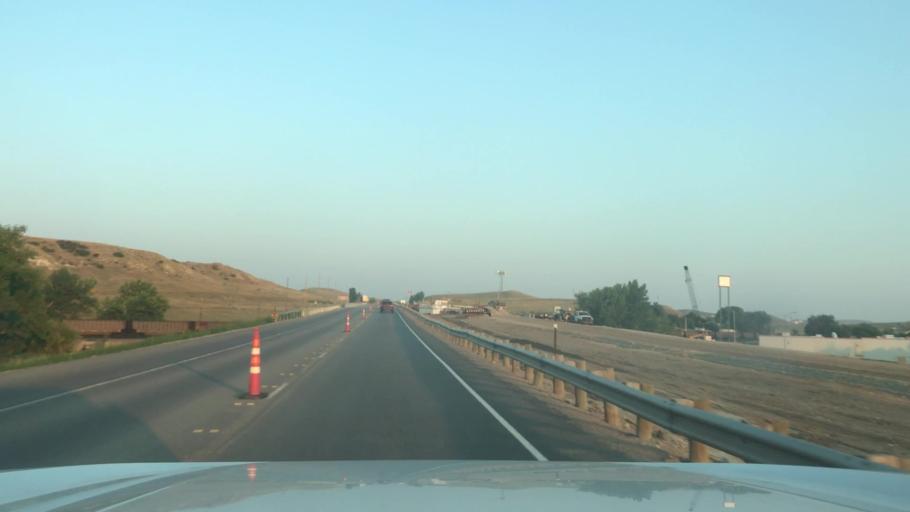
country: US
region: Wyoming
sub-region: Sheridan County
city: Sheridan
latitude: 44.8308
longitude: -106.9580
